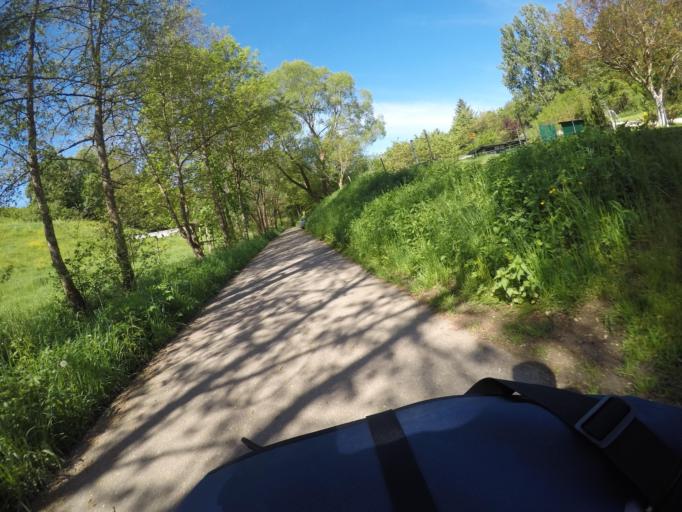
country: DE
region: Baden-Wuerttemberg
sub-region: Regierungsbezirk Stuttgart
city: Huttlingen
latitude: 48.8703
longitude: 10.0901
